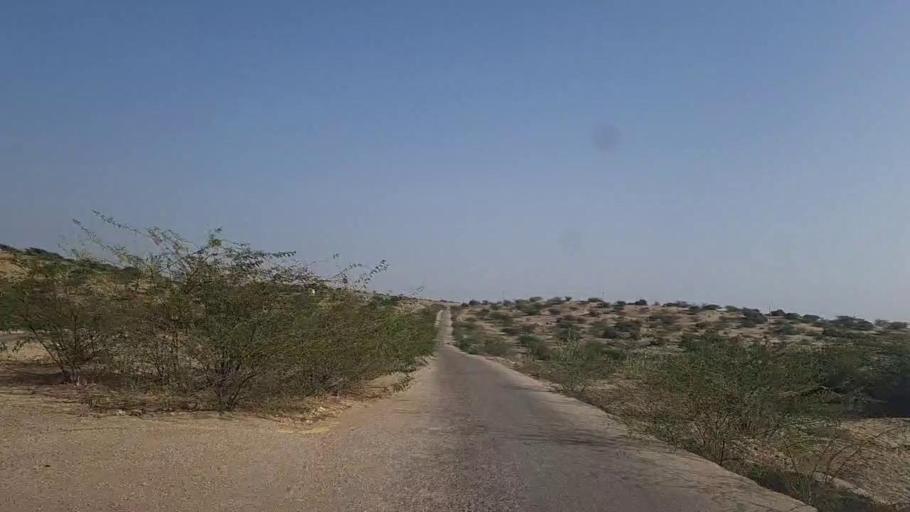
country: PK
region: Sindh
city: Naukot
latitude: 24.6261
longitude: 69.3664
